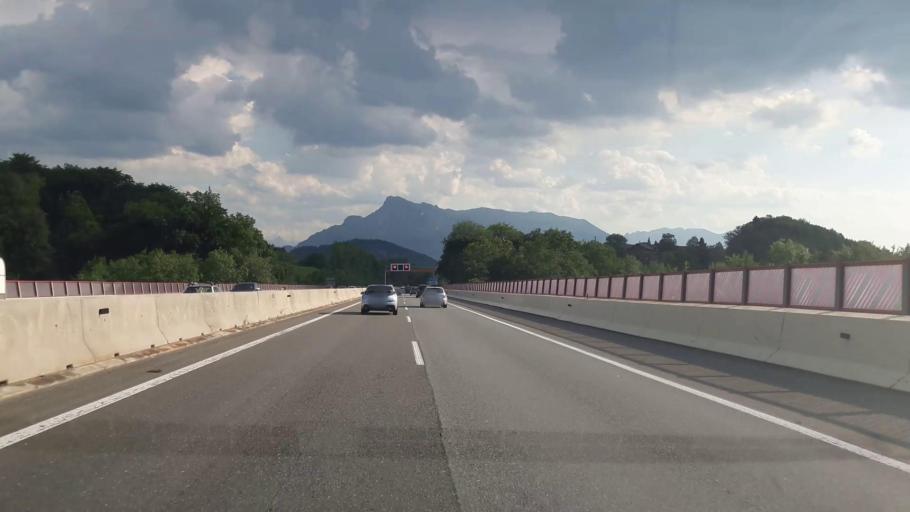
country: AT
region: Salzburg
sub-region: Politischer Bezirk Salzburg-Umgebung
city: Hallwang
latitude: 47.8368
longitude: 13.0741
